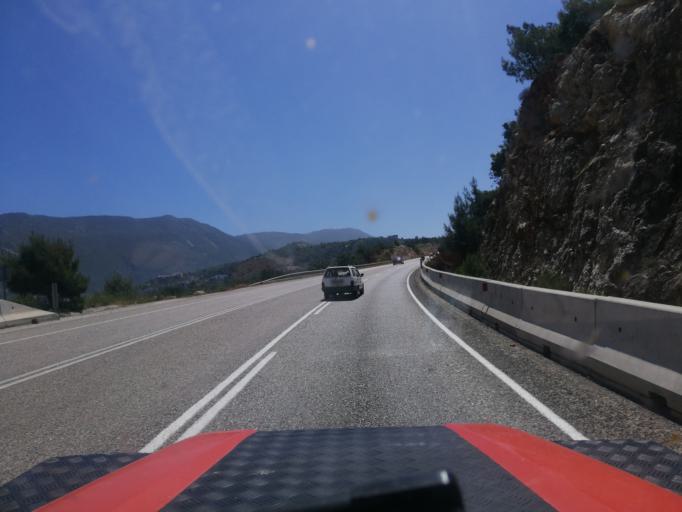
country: TR
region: Antalya
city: Kalkan
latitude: 36.2784
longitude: 29.3886
